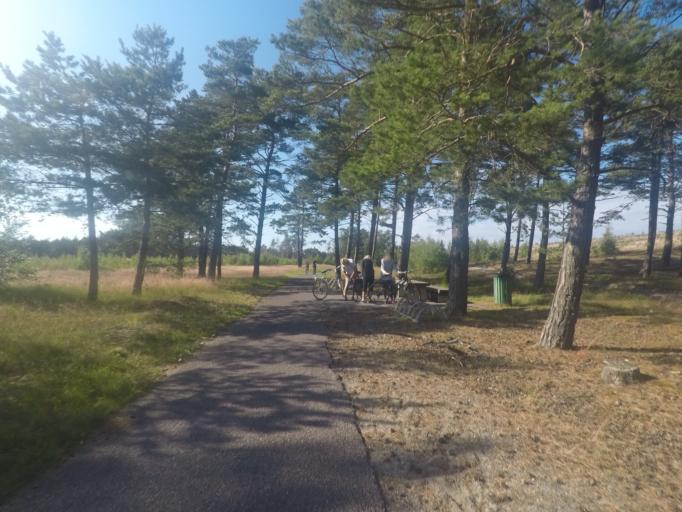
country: LT
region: Klaipedos apskritis
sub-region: Klaipeda
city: Klaipeda
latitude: 55.5858
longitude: 21.1133
